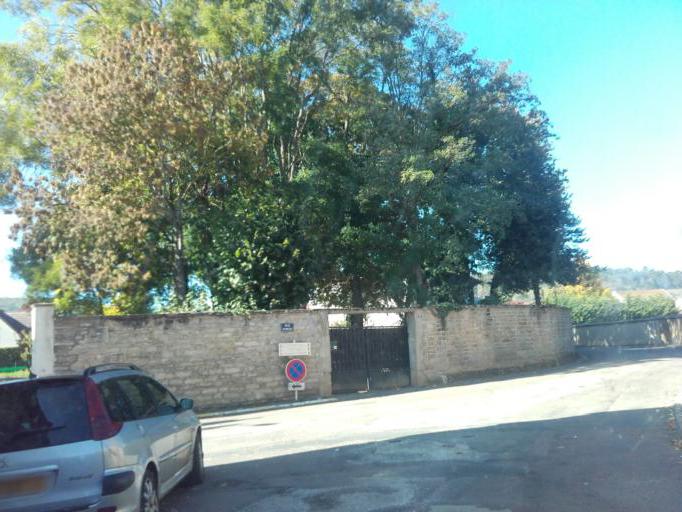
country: FR
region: Bourgogne
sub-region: Departement de la Cote-d'Or
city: Couchey
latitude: 47.2611
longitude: 4.9783
